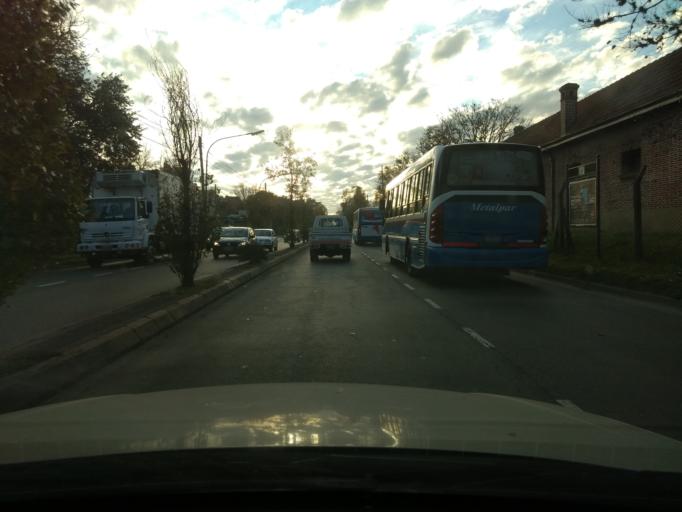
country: AR
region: Buenos Aires
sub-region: Partido de San Isidro
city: San Isidro
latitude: -34.4915
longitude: -58.5457
